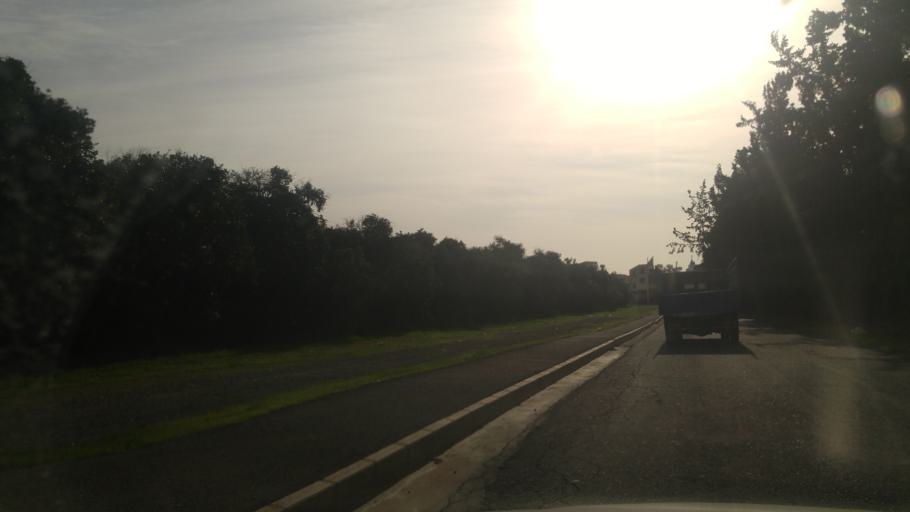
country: CY
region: Limassol
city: Pano Polemidia
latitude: 34.6625
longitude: 32.9998
